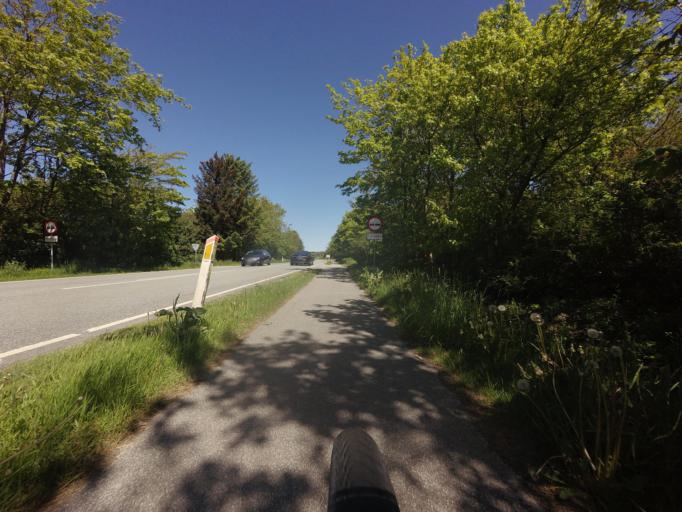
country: DK
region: North Denmark
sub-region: Jammerbugt Kommune
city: Pandrup
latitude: 57.3142
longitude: 9.7072
